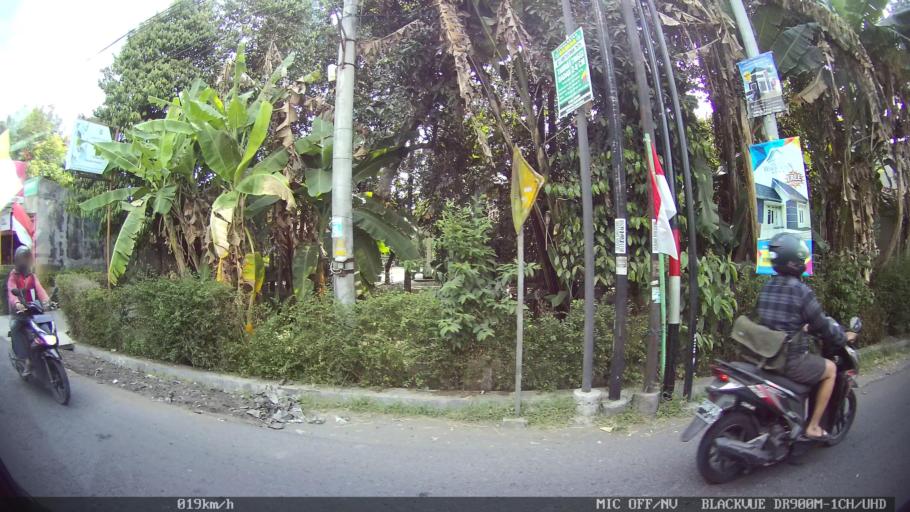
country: ID
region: Daerah Istimewa Yogyakarta
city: Kasihan
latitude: -7.8229
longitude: 110.3282
